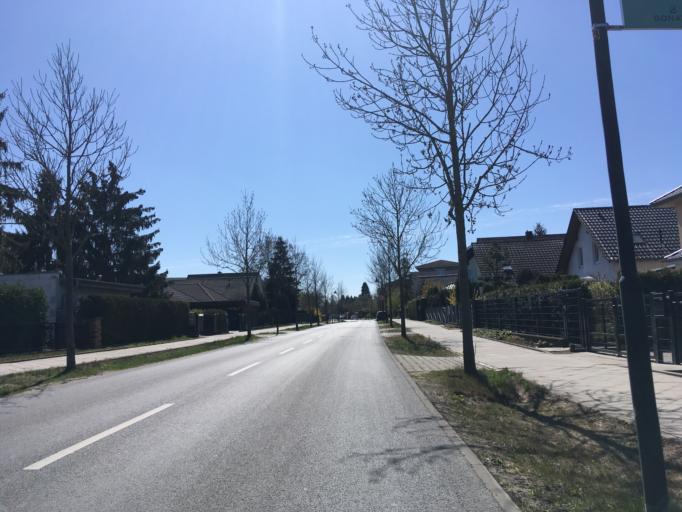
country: DE
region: Brandenburg
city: Bernau bei Berlin
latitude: 52.6738
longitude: 13.5559
